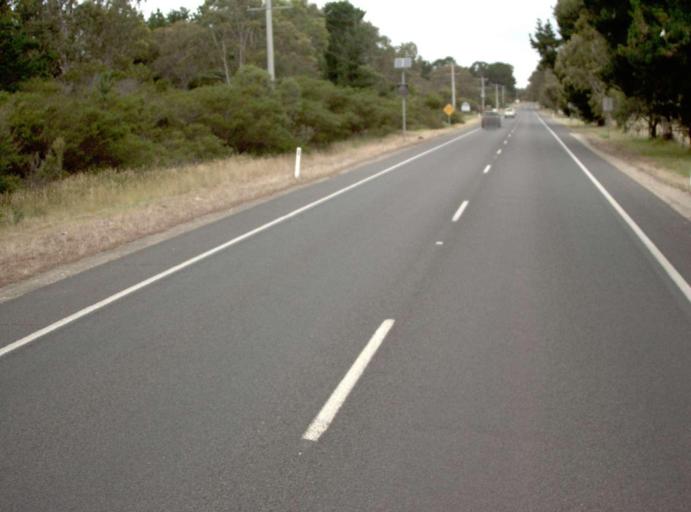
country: AU
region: Victoria
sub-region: Wellington
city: Sale
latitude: -38.1674
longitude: 147.0871
